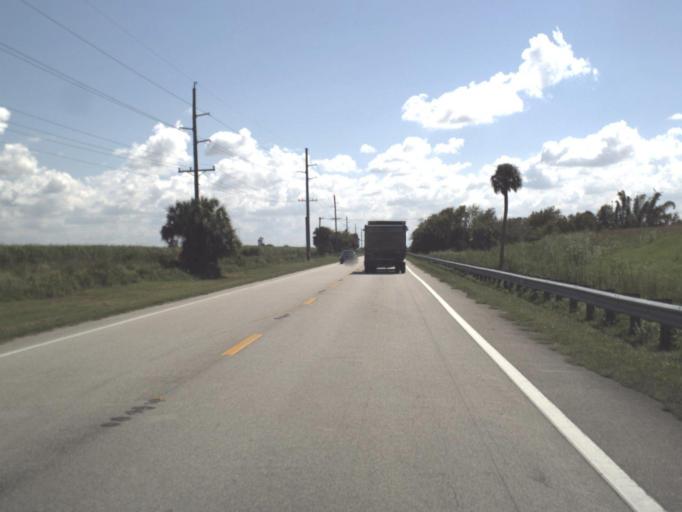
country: US
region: Florida
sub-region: Glades County
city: Moore Haven
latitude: 26.8723
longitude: -81.1227
